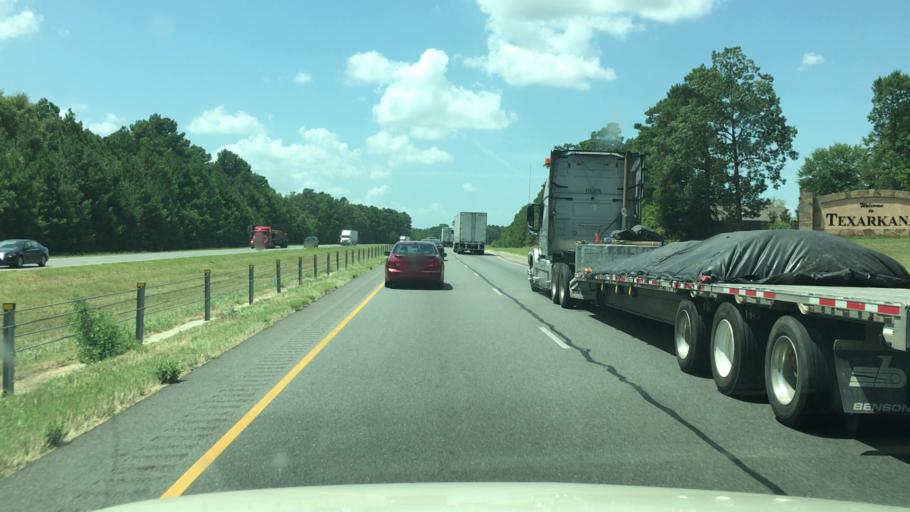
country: US
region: Arkansas
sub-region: Miller County
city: Texarkana
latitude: 33.4861
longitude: -93.9755
